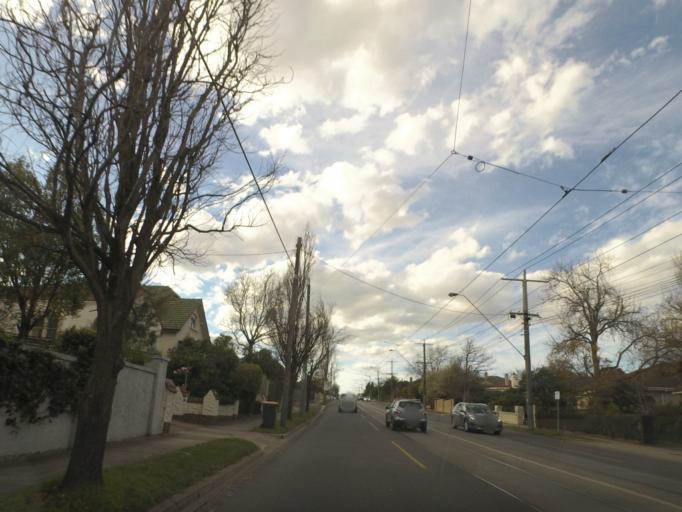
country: AU
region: Victoria
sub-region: Stonnington
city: Glen Iris
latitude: -37.8494
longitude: 145.0531
